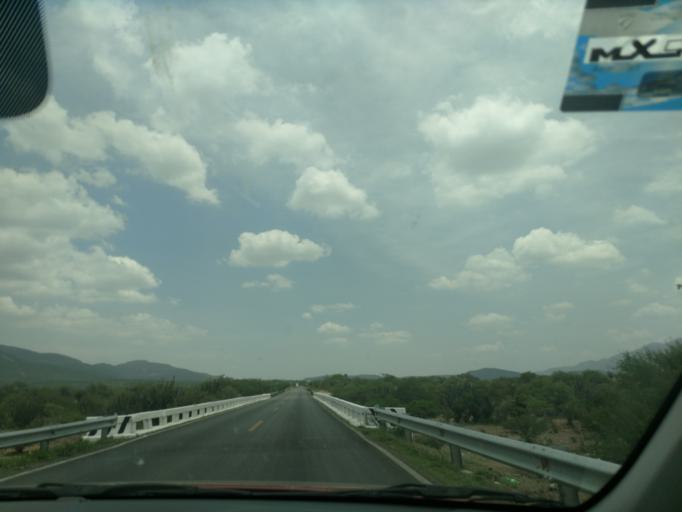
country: MX
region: San Luis Potosi
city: Villa Juarez
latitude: 22.0185
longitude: -100.3943
